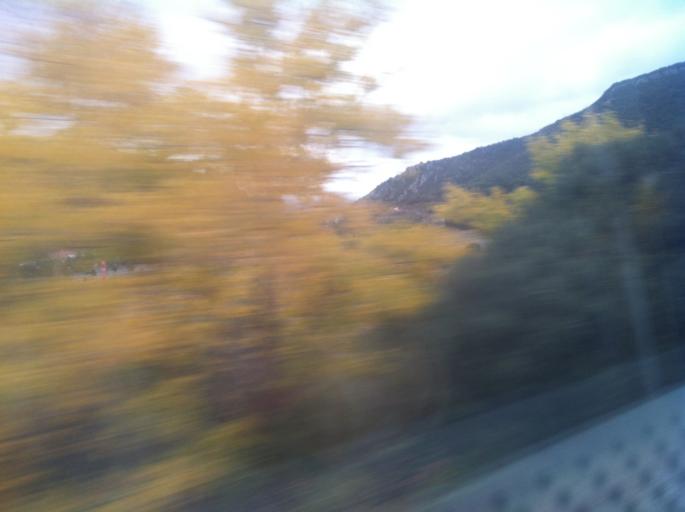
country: ES
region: Castille and Leon
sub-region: Provincia de Burgos
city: Ameyugo
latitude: 42.6486
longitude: -3.0729
